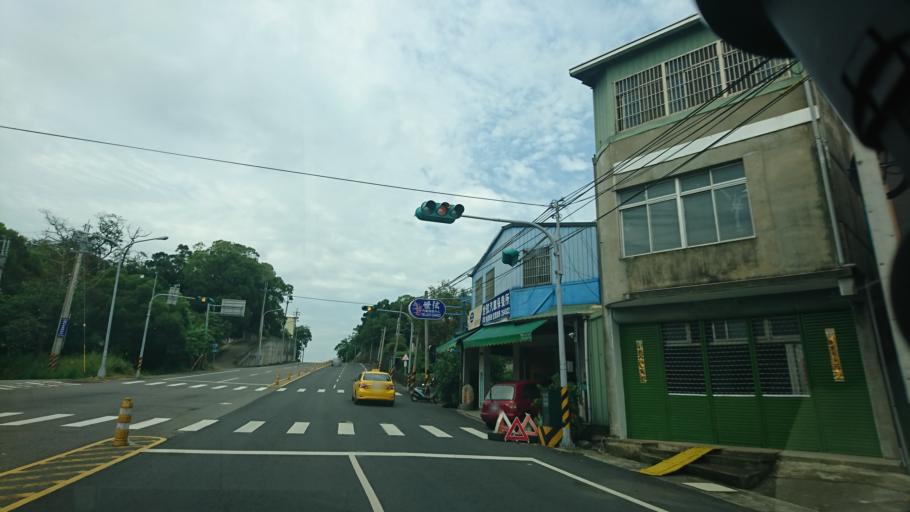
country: TW
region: Taiwan
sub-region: Miaoli
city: Miaoli
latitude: 24.5287
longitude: 120.7994
